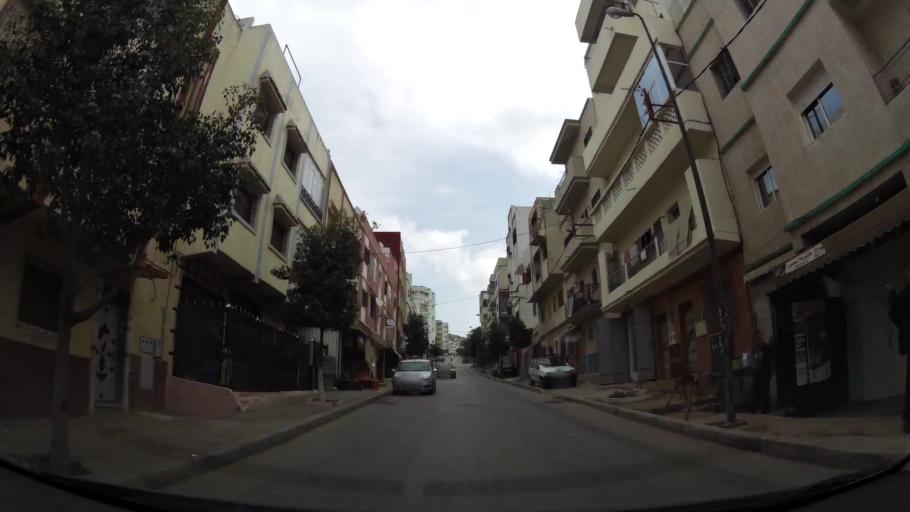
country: MA
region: Tanger-Tetouan
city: Tetouan
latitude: 35.5721
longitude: -5.3928
